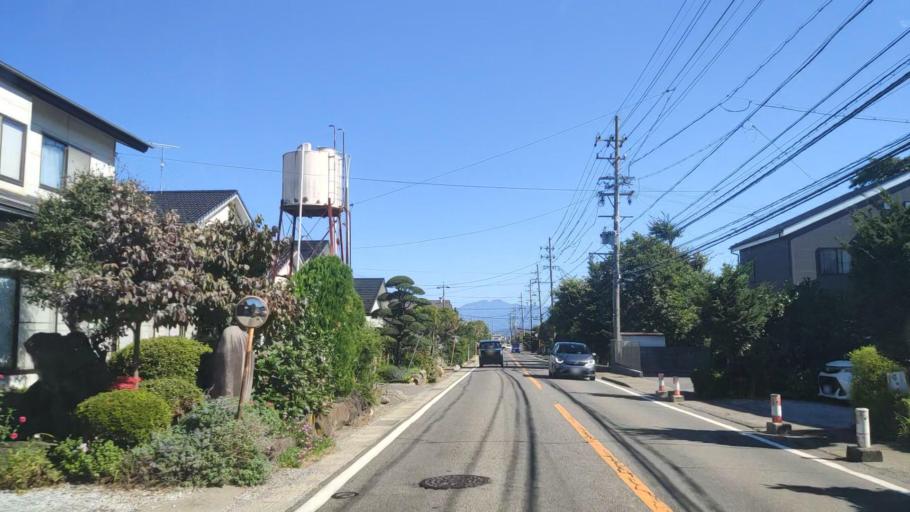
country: JP
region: Nagano
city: Shiojiri
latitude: 36.1422
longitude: 137.9413
